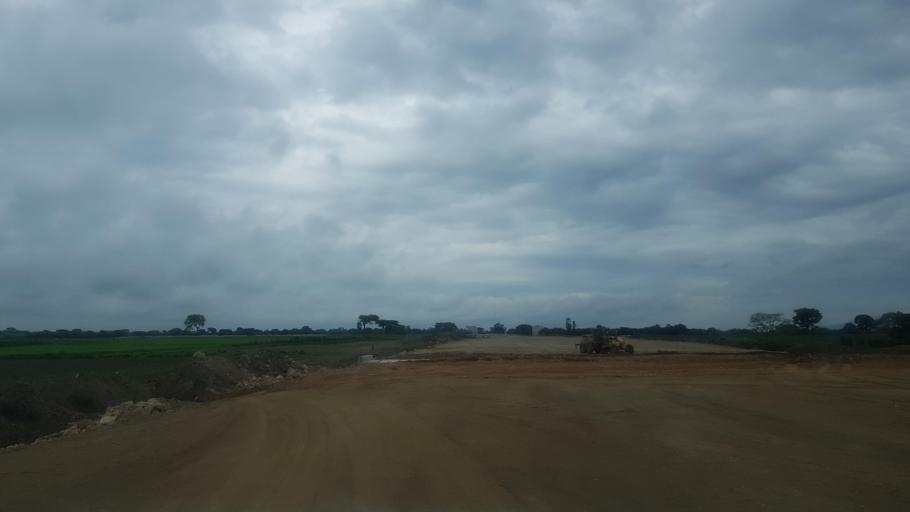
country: ET
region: Oromiya
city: Shashemene
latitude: 7.3594
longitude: 38.6416
